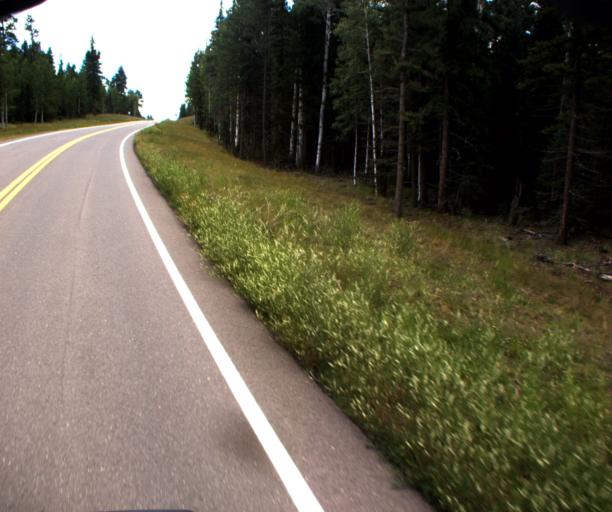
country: US
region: Arizona
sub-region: Apache County
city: Eagar
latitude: 33.9805
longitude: -109.5017
